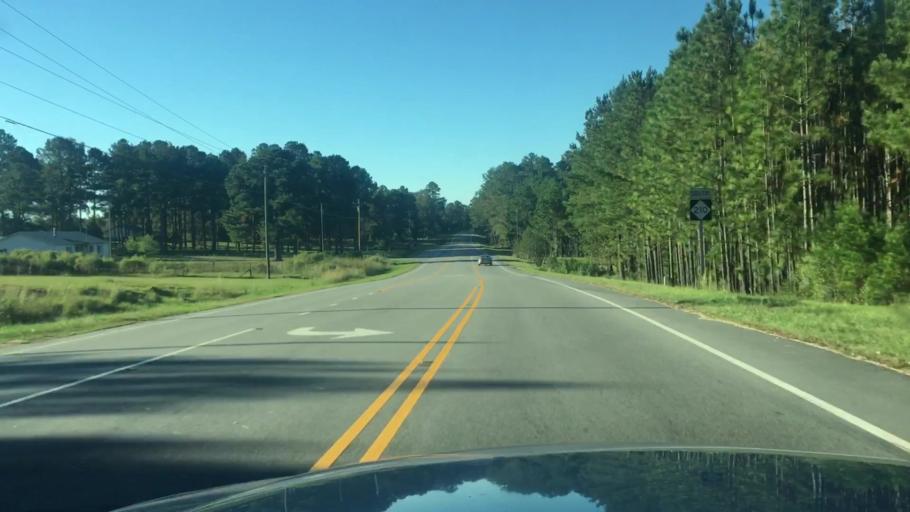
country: US
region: North Carolina
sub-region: Cumberland County
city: Spring Lake
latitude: 35.2647
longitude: -78.9220
